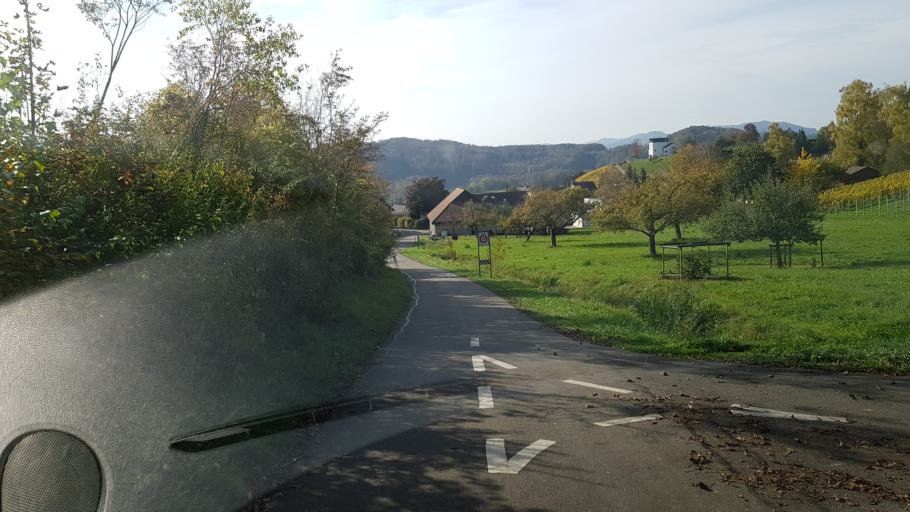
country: CH
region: Aargau
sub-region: Bezirk Baden
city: Birmenstorf
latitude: 47.4642
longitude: 8.2514
